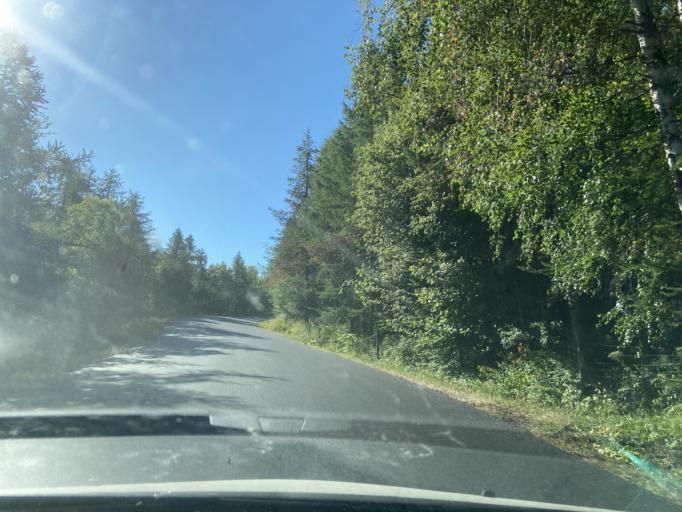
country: FR
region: Provence-Alpes-Cote d'Azur
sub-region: Departement des Hautes-Alpes
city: Guillestre
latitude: 44.6398
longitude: 6.6272
